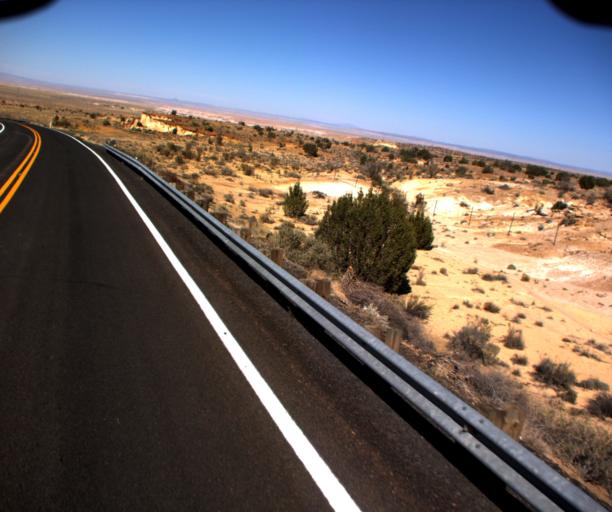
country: US
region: Arizona
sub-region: Coconino County
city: Tuba City
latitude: 35.9271
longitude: -110.8885
